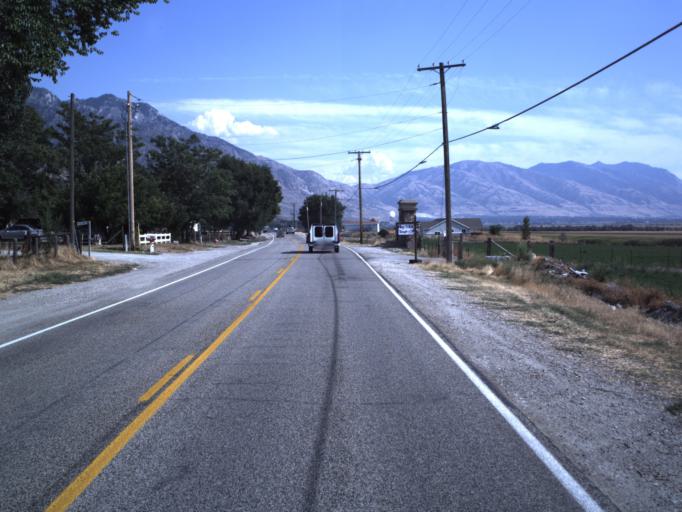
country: US
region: Utah
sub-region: Box Elder County
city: Honeyville
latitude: 41.6069
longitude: -112.0592
